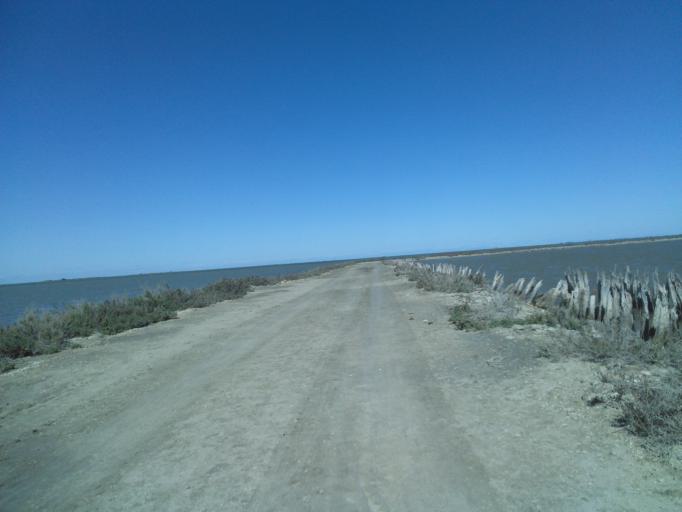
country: FR
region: Provence-Alpes-Cote d'Azur
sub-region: Departement des Bouches-du-Rhone
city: Saintes-Maries-de-la-Mer
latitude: 43.4300
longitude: 4.6173
